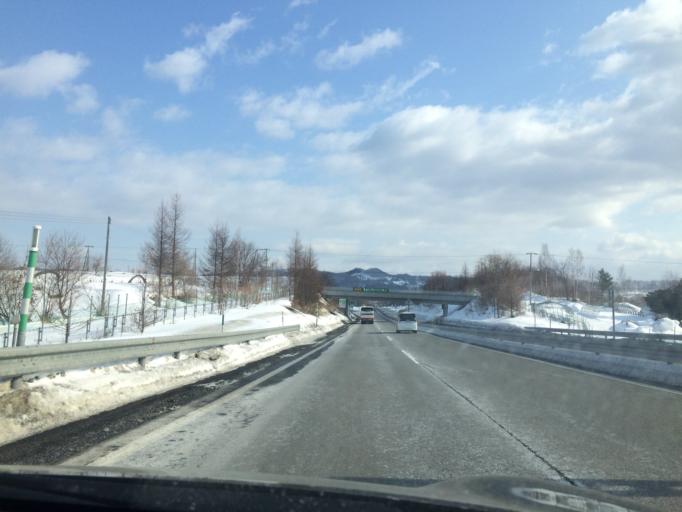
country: JP
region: Hokkaido
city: Chitose
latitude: 42.9042
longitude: 141.8949
